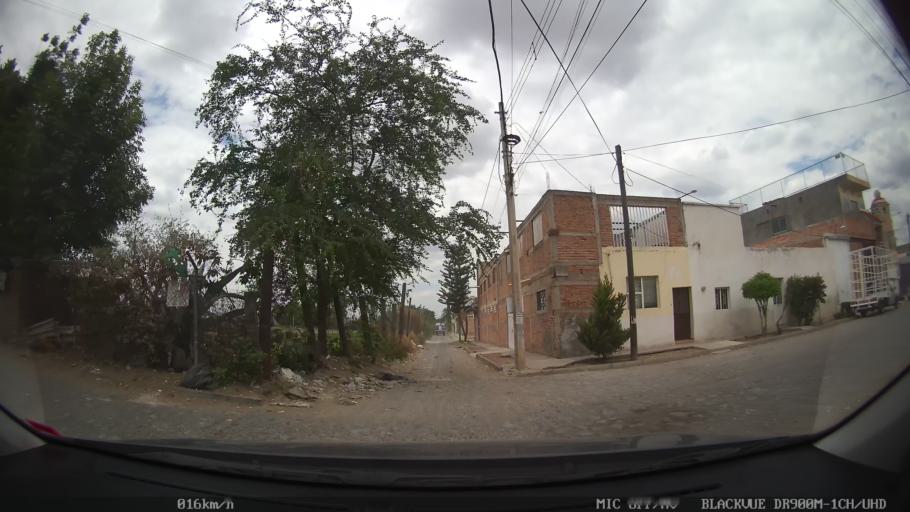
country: MX
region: Jalisco
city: Tlaquepaque
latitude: 20.6478
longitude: -103.2645
